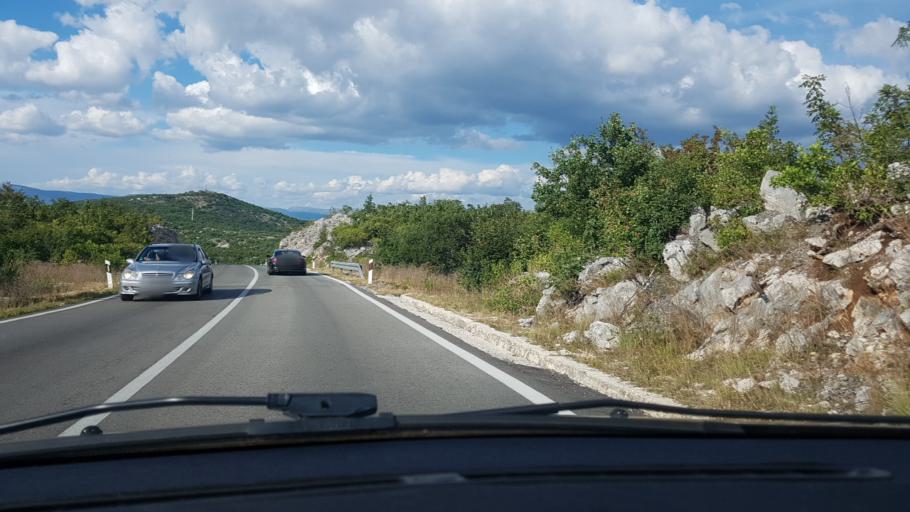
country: HR
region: Splitsko-Dalmatinska
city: Grubine
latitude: 43.4090
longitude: 17.0910
